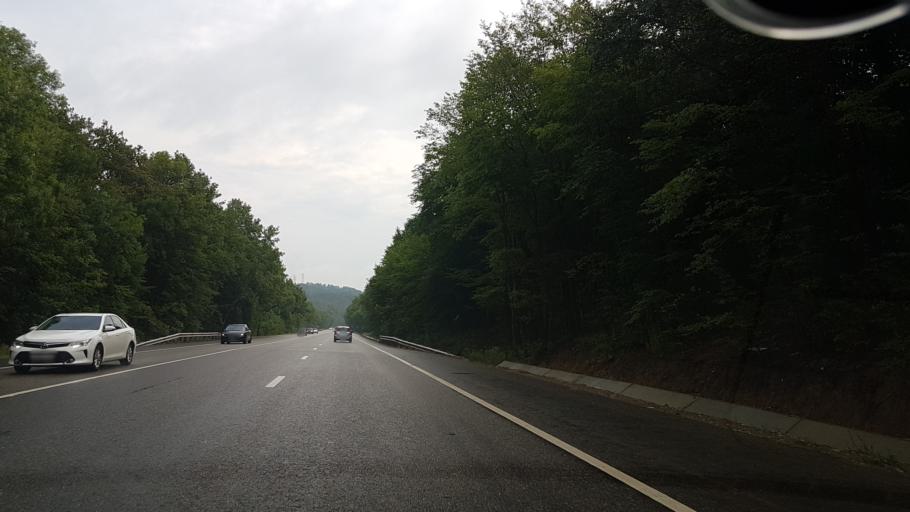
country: RU
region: Krasnodarskiy
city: Dzhubga
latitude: 44.4096
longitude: 38.7389
